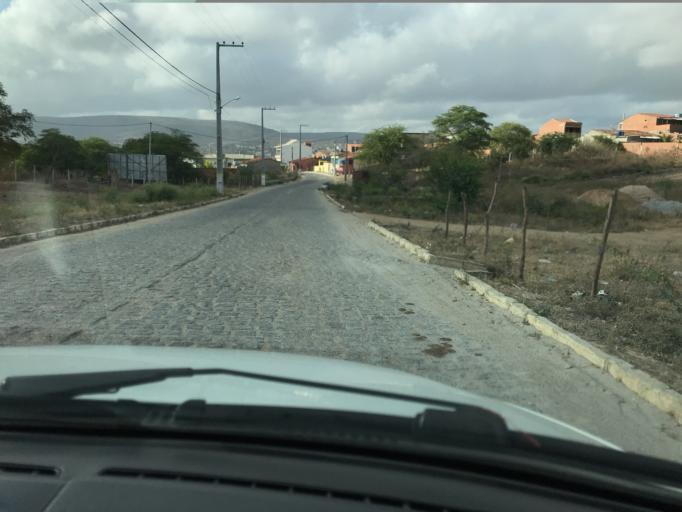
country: BR
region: Pernambuco
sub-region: Bezerros
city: Bezerros
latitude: -8.2194
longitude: -35.7522
